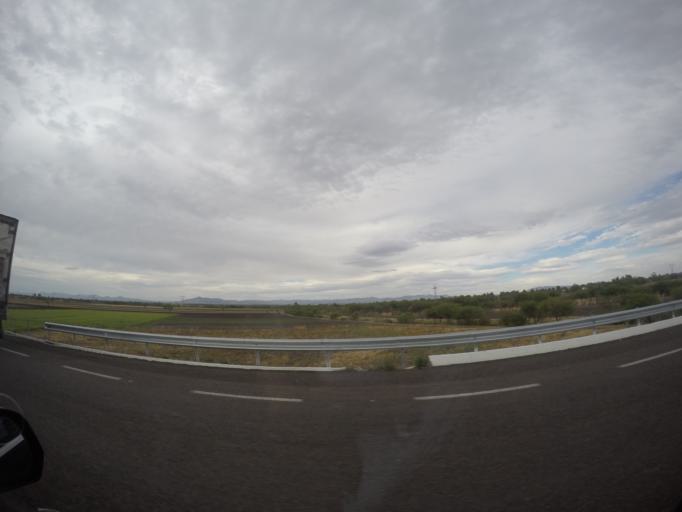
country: MX
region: Guanajuato
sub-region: Irapuato
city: Serrano
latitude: 20.8085
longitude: -101.4353
